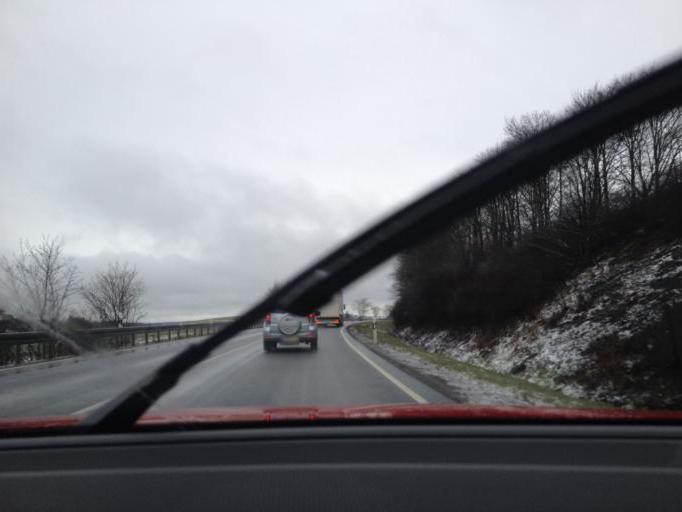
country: DE
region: Bavaria
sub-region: Upper Franconia
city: Dohlau
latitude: 50.2760
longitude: 11.9660
